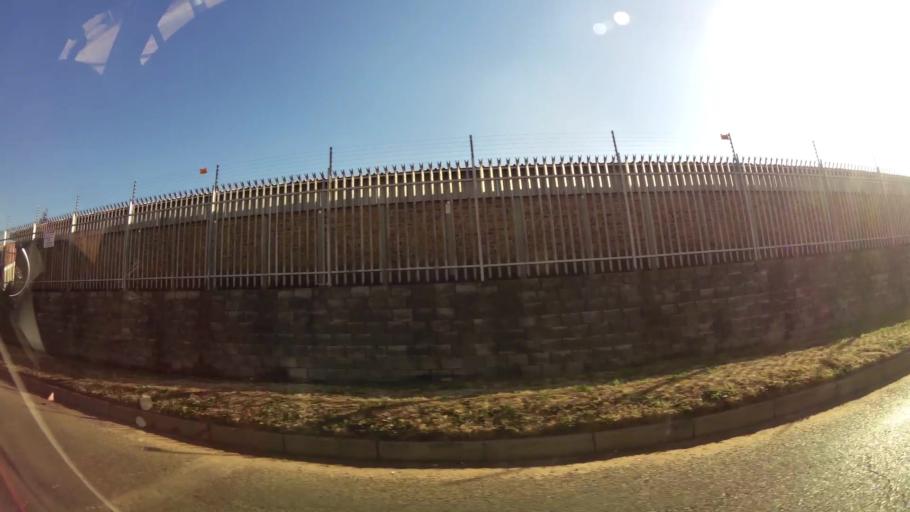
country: ZA
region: Gauteng
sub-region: City of Johannesburg Metropolitan Municipality
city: Roodepoort
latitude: -26.1540
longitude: 27.8528
